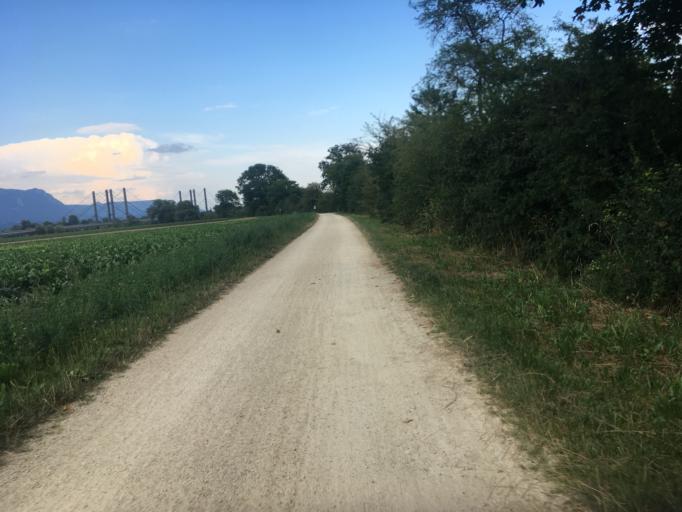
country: CH
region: Bern
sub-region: Seeland District
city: Arch
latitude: 47.1738
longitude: 7.4257
